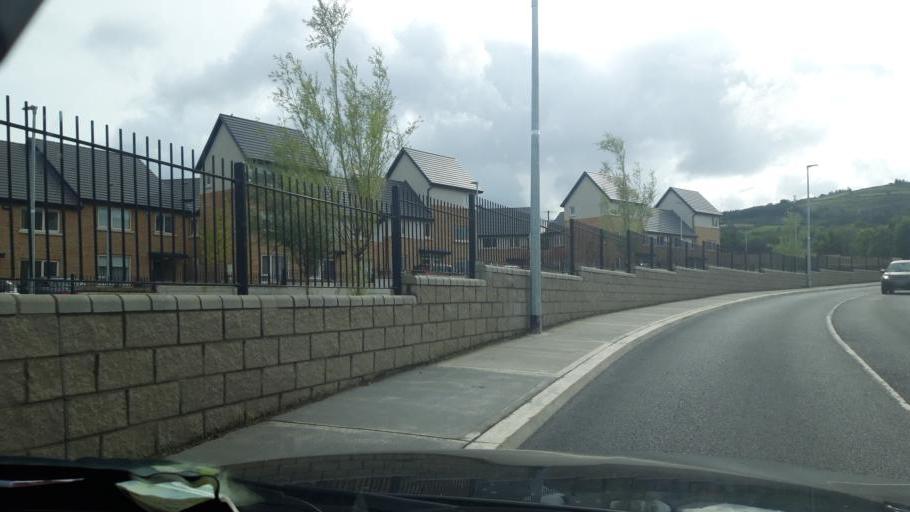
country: IE
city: Knocklyon
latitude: 53.2697
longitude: -6.3266
